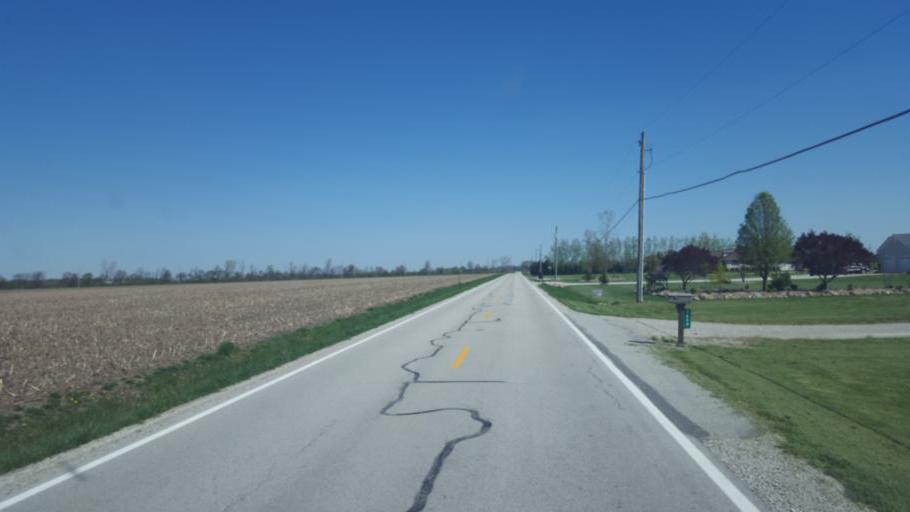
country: US
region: Ohio
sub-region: Sandusky County
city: Stony Prairie
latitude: 41.2949
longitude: -83.1973
